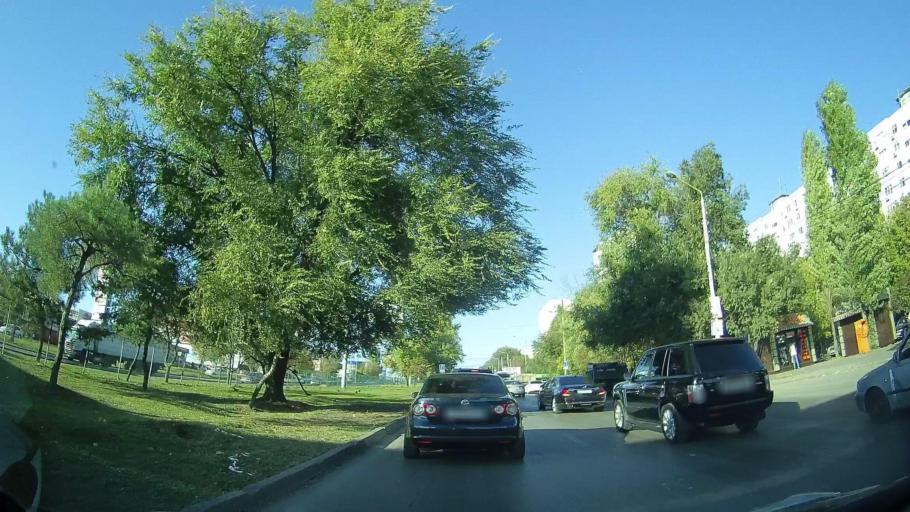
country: RU
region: Rostov
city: Kalinin
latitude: 47.2295
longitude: 39.6140
